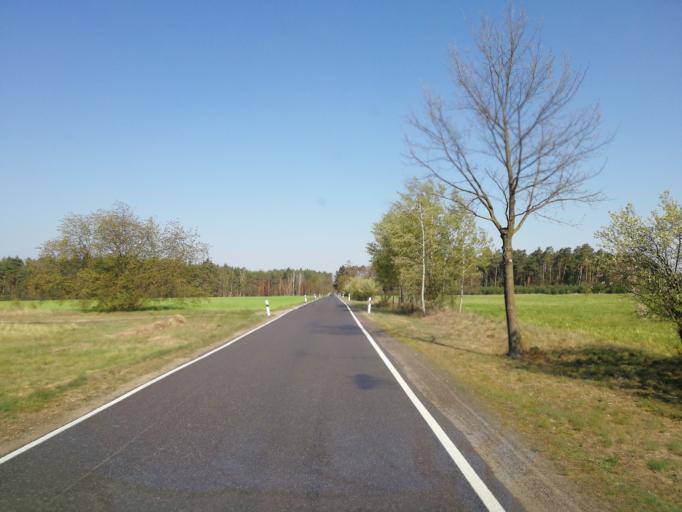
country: DE
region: Brandenburg
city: Bronkow
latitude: 51.7055
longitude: 13.8755
